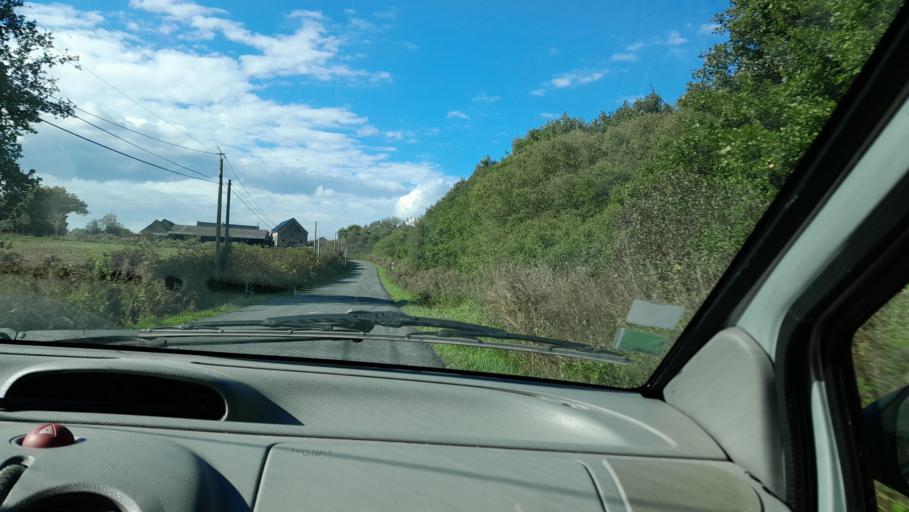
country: FR
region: Pays de la Loire
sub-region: Departement de la Mayenne
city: Ahuille
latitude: 48.0340
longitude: -0.8952
